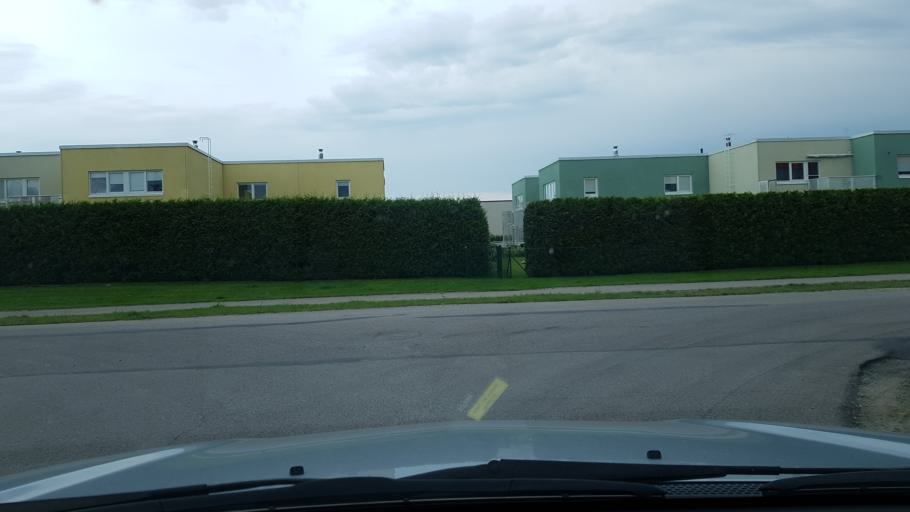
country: EE
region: Harju
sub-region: Rae vald
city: Jueri
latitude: 59.3481
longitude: 24.8981
